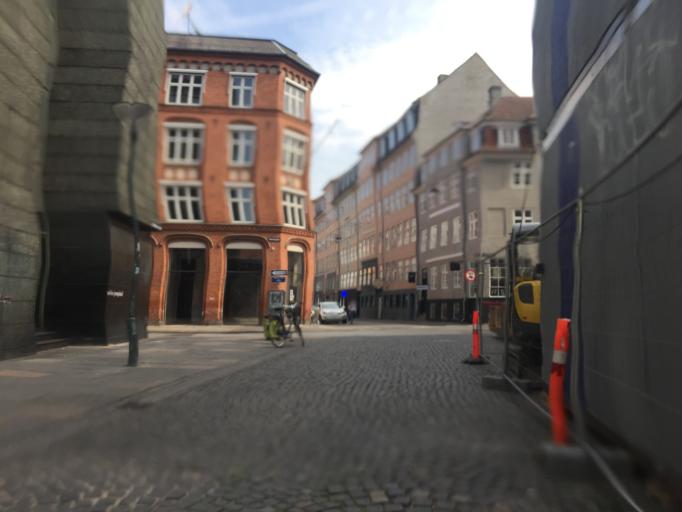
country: DK
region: Capital Region
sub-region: Kobenhavn
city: Copenhagen
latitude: 55.6815
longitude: 12.5786
